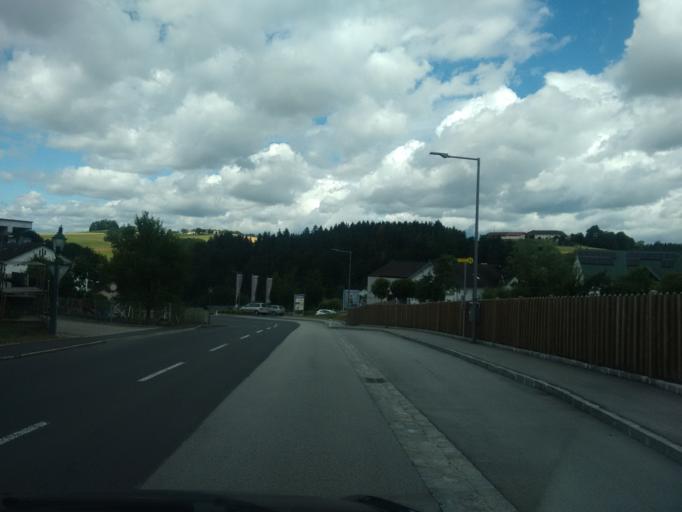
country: AT
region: Upper Austria
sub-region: Politischer Bezirk Urfahr-Umgebung
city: Gramastetten
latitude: 48.3813
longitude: 14.1917
